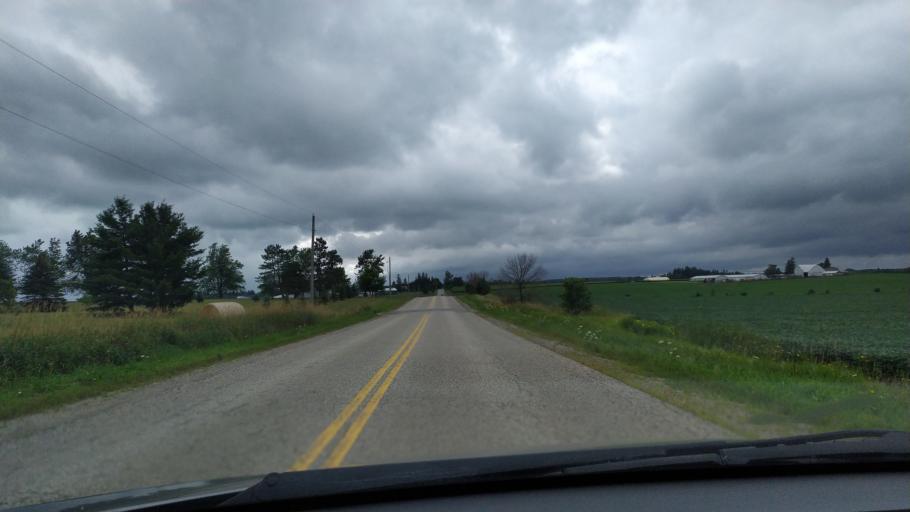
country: CA
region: Ontario
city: Kitchener
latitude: 43.3369
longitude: -80.6180
